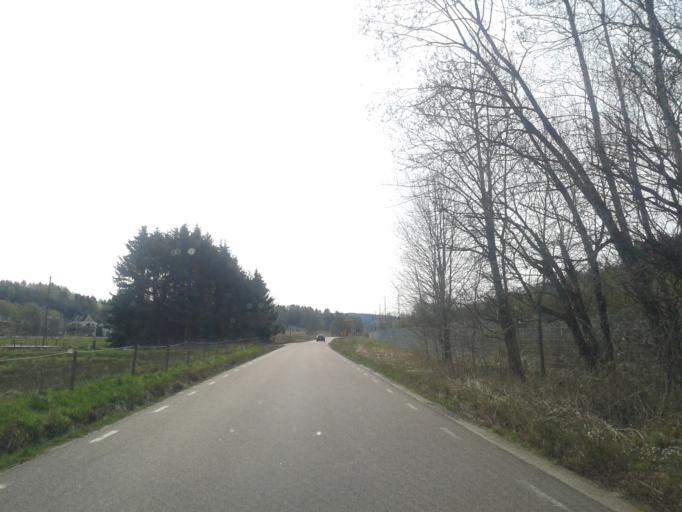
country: SE
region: Vaestra Goetaland
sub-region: Kungalvs Kommun
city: Kode
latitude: 57.9054
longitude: 11.8955
